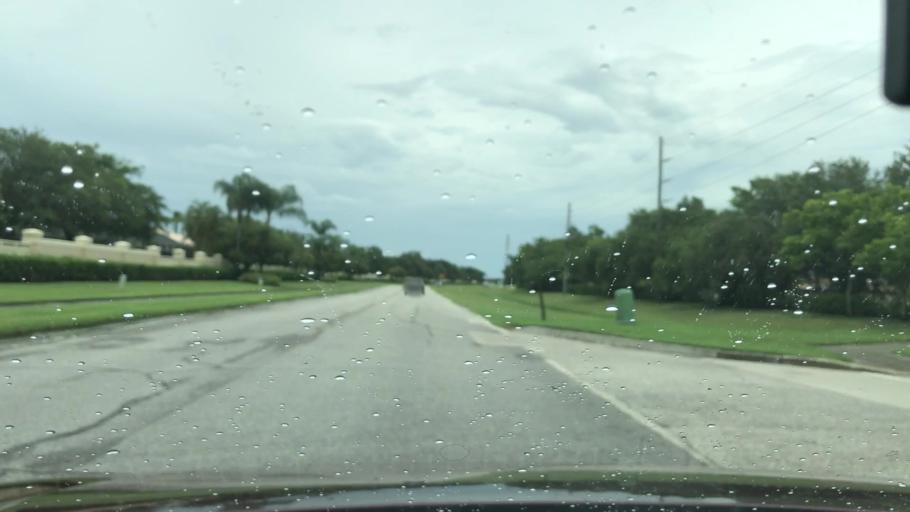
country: US
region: Florida
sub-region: Sarasota County
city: Lake Sarasota
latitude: 27.3082
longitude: -82.3956
